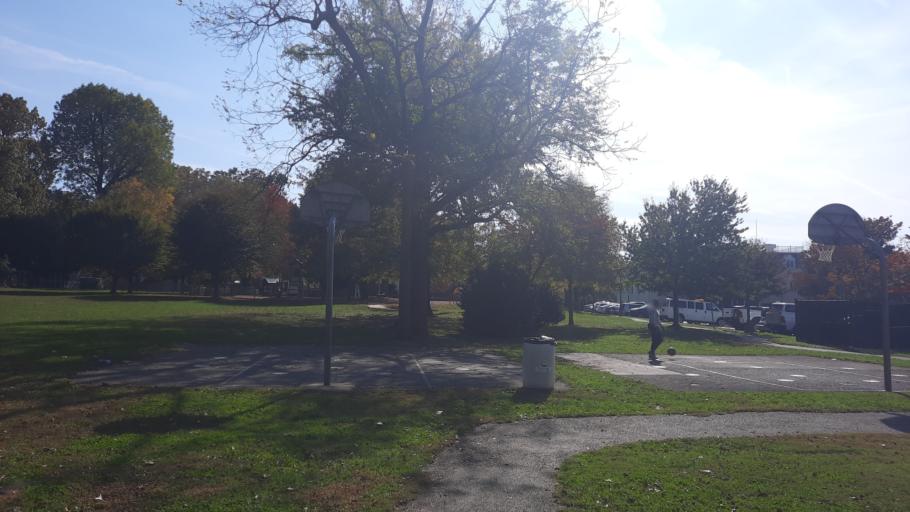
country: US
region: Maryland
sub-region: Montgomery County
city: Gaithersburg
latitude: 39.1409
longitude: -77.1919
